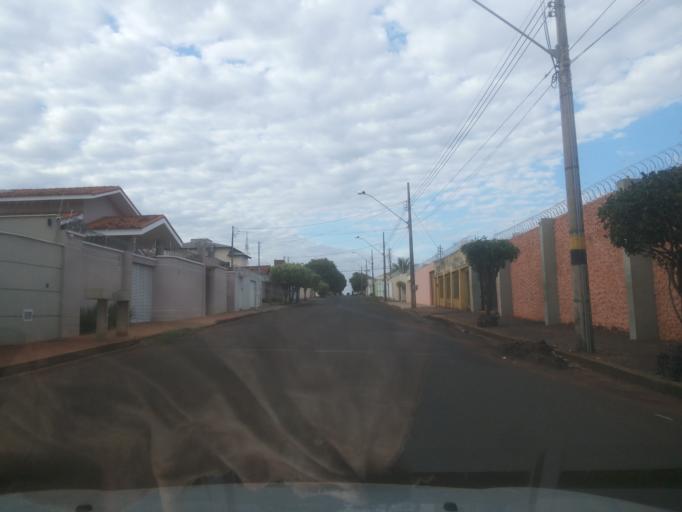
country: BR
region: Minas Gerais
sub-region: Ituiutaba
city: Ituiutaba
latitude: -18.9895
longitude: -49.4584
